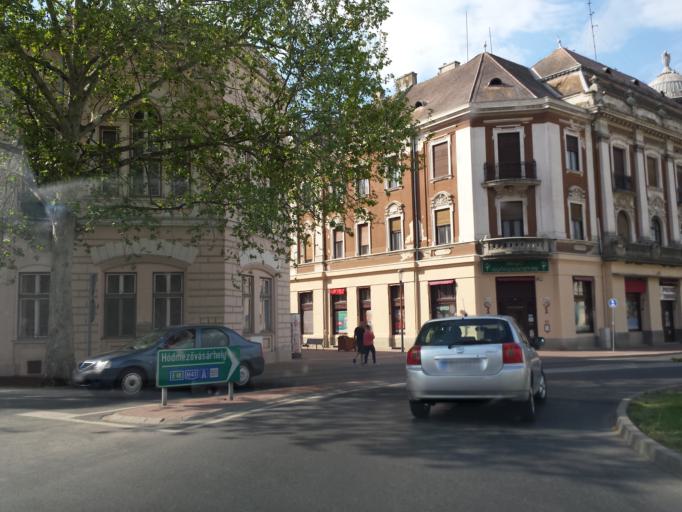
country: HU
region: Csongrad
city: Mako
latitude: 46.2149
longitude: 20.4747
